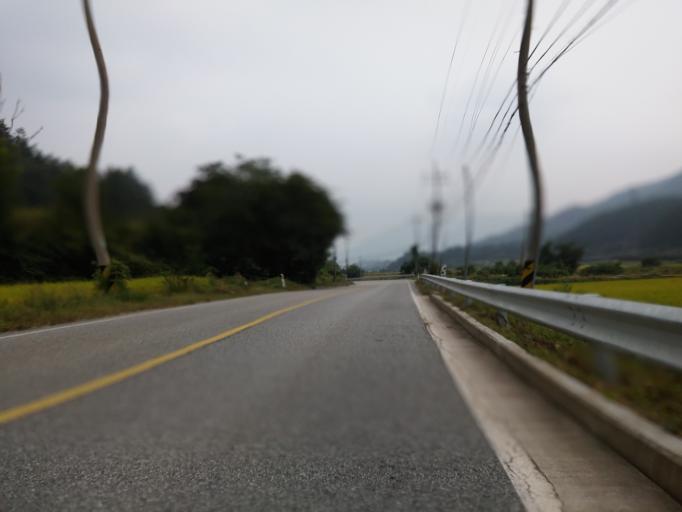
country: KR
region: Chungcheongbuk-do
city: Okcheon
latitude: 36.3937
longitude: 127.7005
